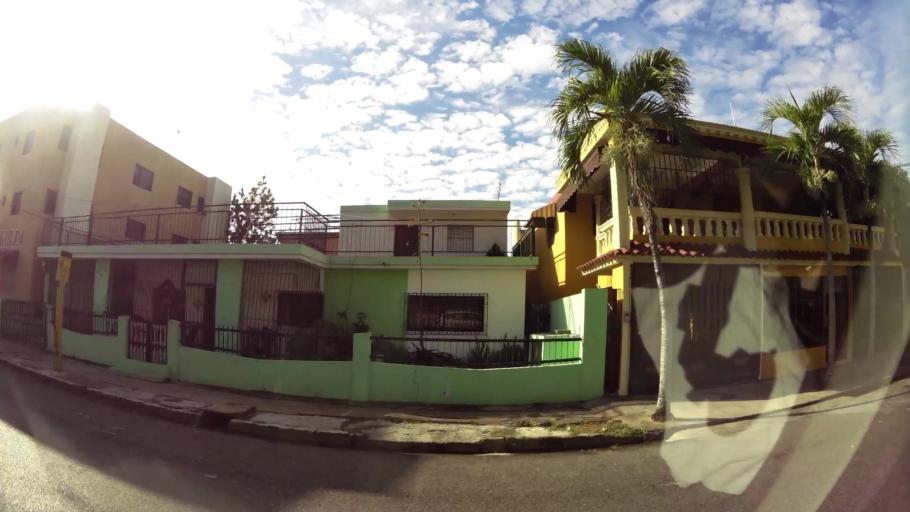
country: DO
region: Santo Domingo
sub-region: Santo Domingo
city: Santo Domingo Este
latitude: 18.4878
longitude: -69.8554
